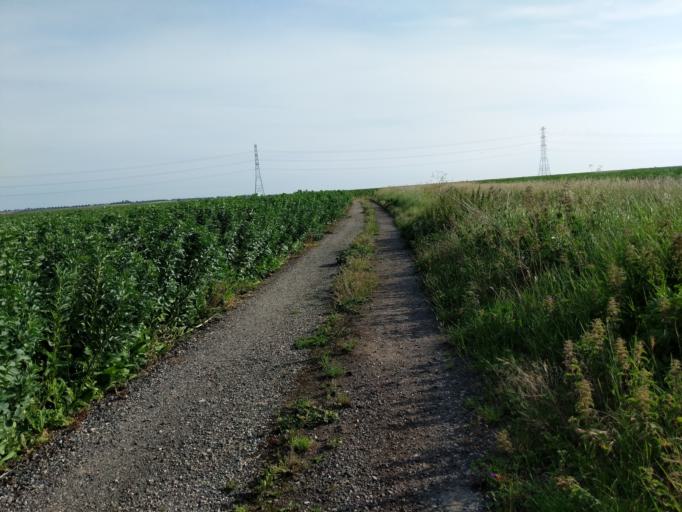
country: GB
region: England
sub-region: Kent
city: Faversham
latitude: 51.3334
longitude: 0.9145
